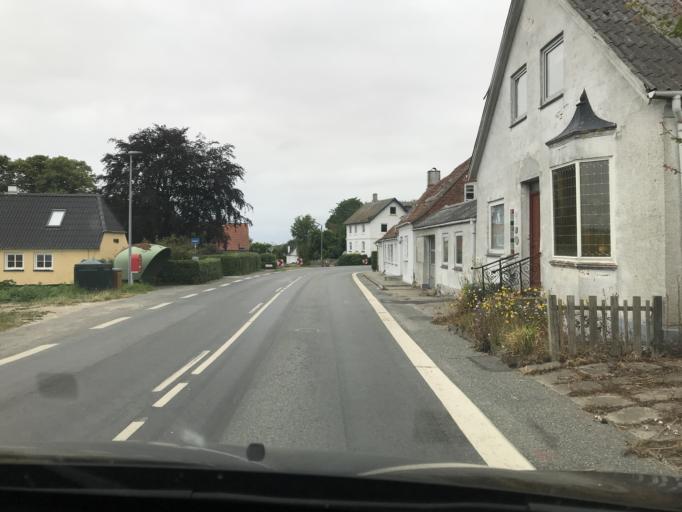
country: DK
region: South Denmark
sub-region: AEro Kommune
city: AEroskobing
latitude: 54.8478
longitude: 10.4206
